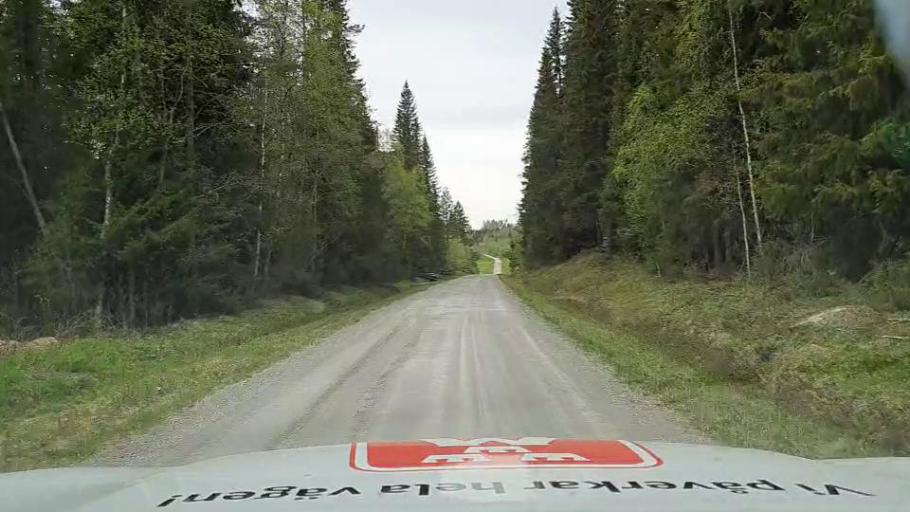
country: SE
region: Jaemtland
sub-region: Bergs Kommun
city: Hoverberg
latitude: 62.6642
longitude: 14.8245
